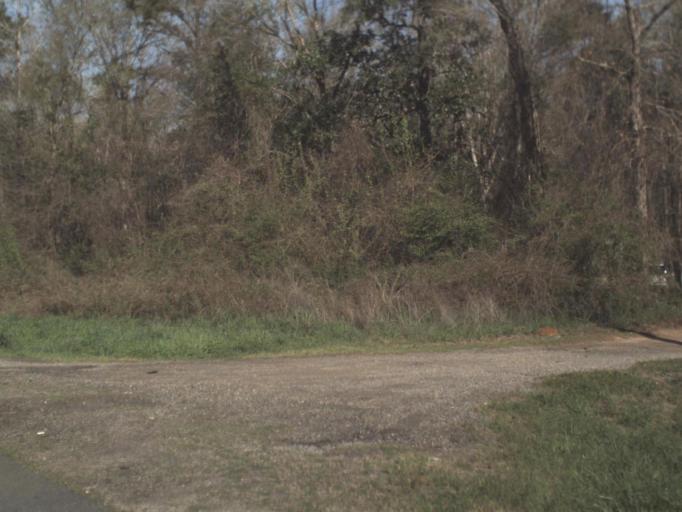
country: US
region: Alabama
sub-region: Houston County
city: Cottonwood
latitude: 30.9346
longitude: -85.3029
